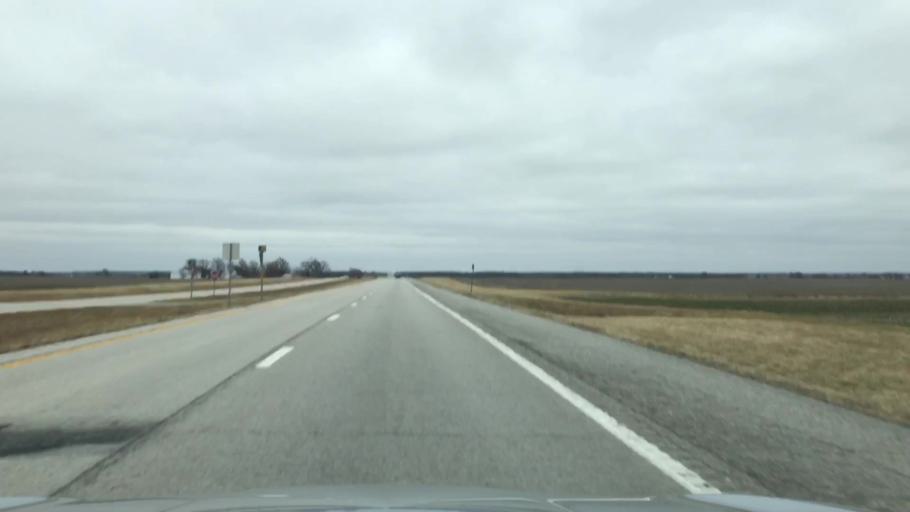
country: US
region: Missouri
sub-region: Livingston County
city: Chillicothe
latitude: 39.7762
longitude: -93.4780
